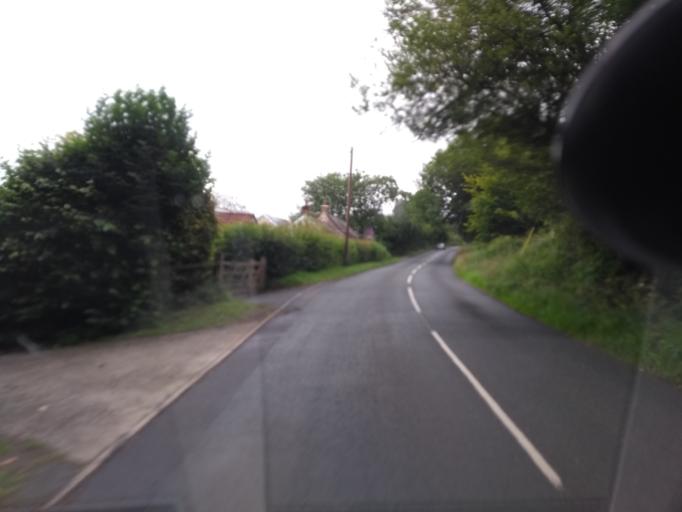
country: GB
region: England
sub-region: Somerset
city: Taunton
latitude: 50.9489
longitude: -3.1232
